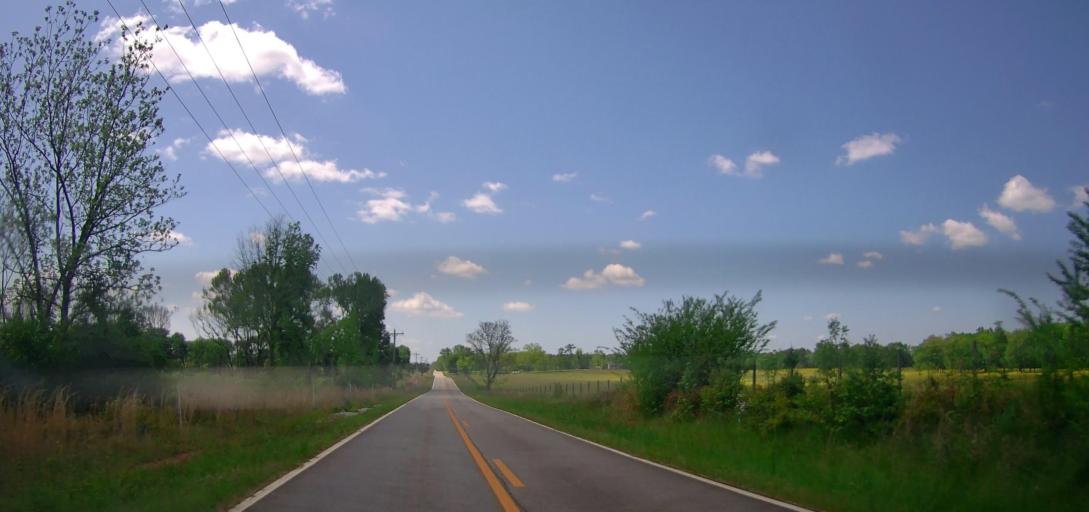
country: US
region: Georgia
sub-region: Putnam County
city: Eatonton
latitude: 33.3280
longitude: -83.3150
